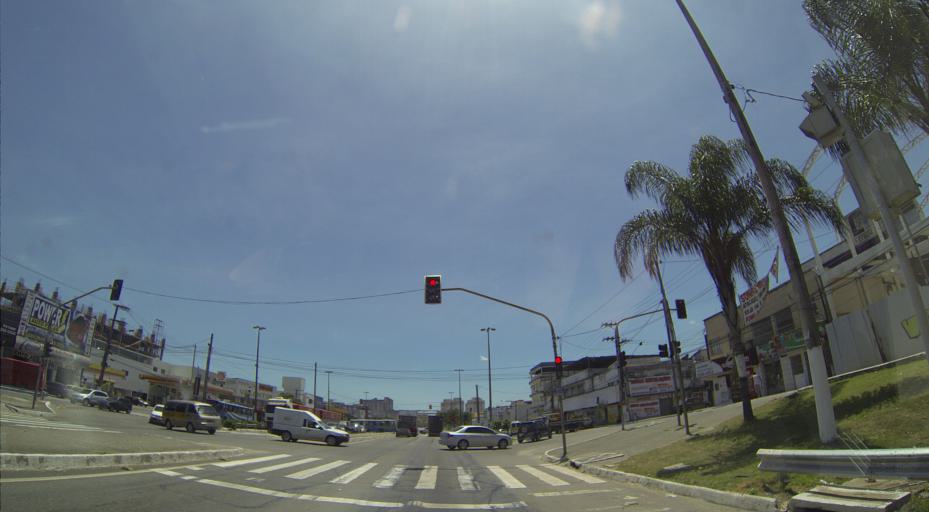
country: BR
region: Espirito Santo
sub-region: Vitoria
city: Vitoria
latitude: -20.3390
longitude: -40.3929
